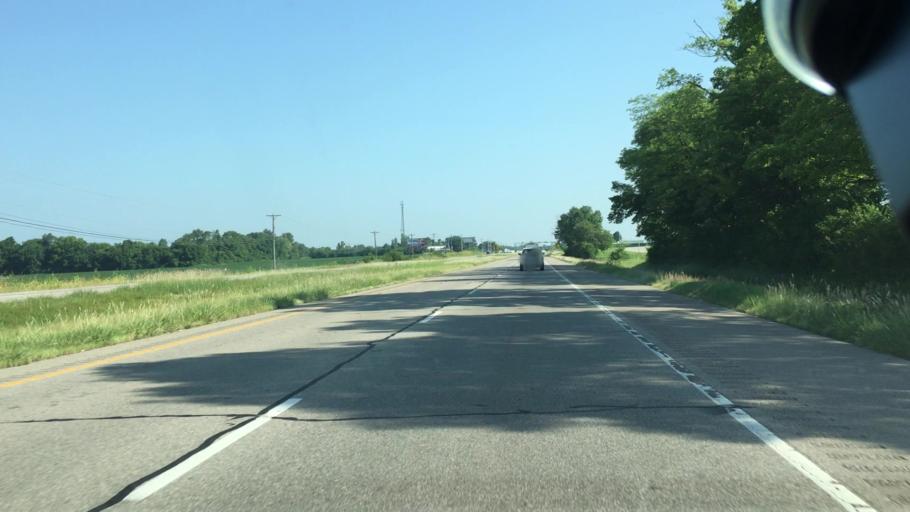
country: US
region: Indiana
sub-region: Gibson County
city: Fort Branch
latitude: 38.2979
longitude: -87.5674
